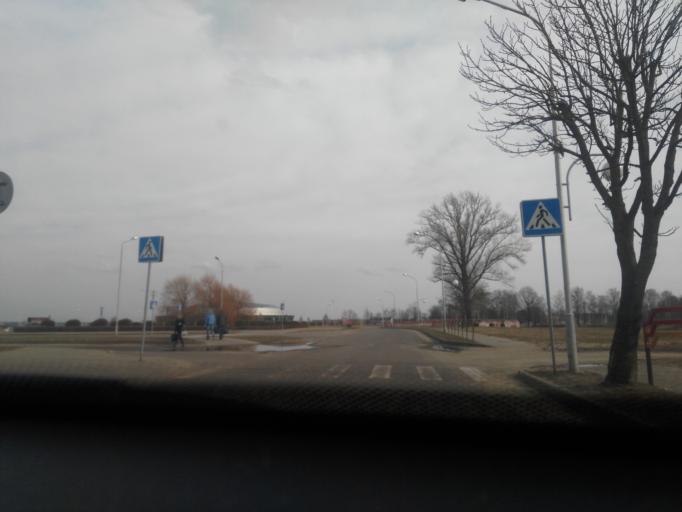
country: BY
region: Mogilev
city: Babruysk
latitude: 53.1433
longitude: 29.2395
